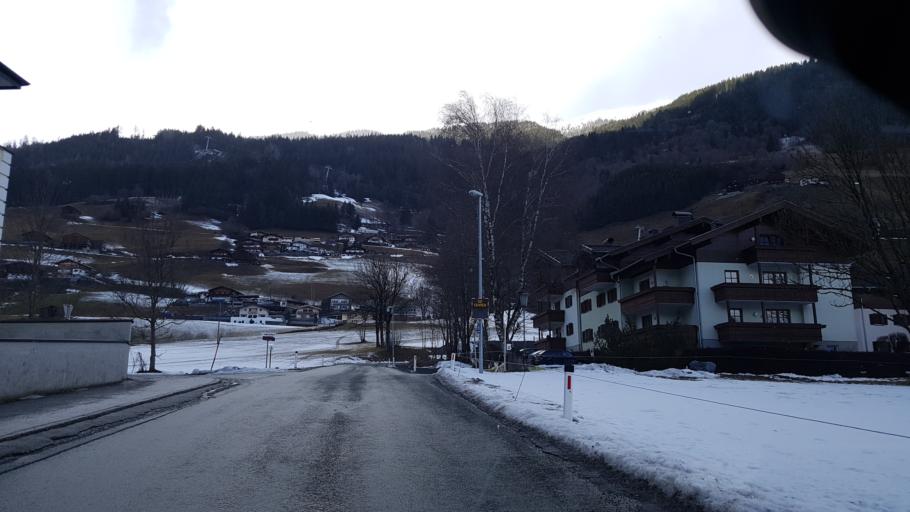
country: AT
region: Salzburg
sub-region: Politischer Bezirk Zell am See
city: Bramberg am Wildkogel
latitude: 47.2689
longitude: 12.3380
